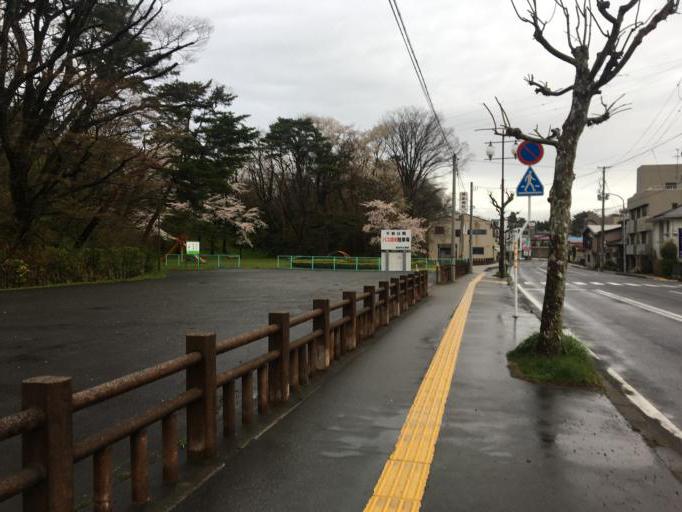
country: JP
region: Akita
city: Akita
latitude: 39.7209
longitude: 140.1257
